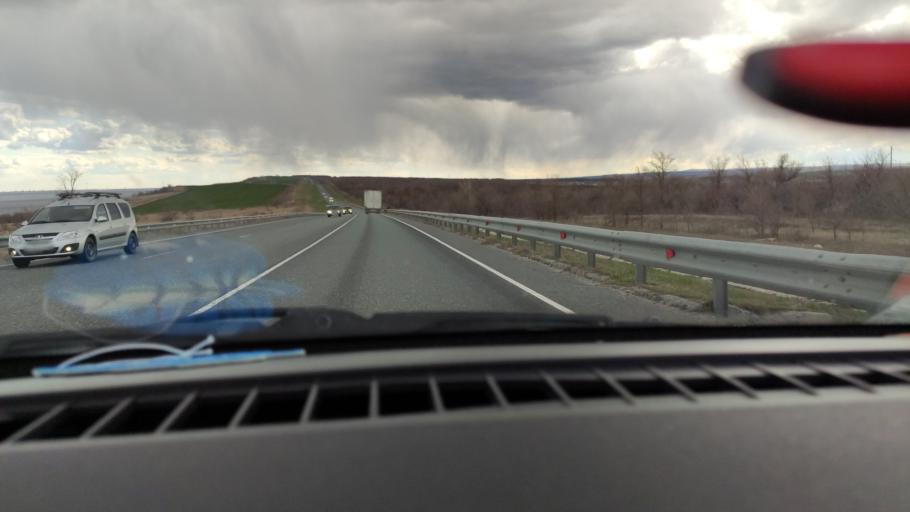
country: RU
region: Saratov
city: Balakovo
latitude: 52.1975
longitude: 47.8604
